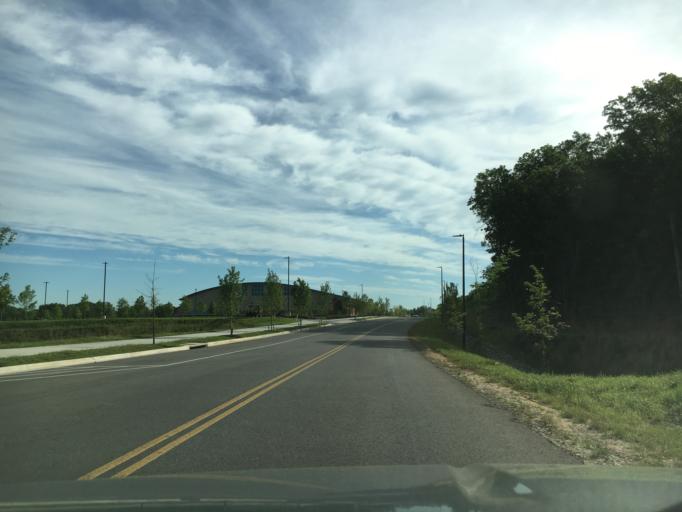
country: US
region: Virginia
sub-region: City of Lynchburg
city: West Lynchburg
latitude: 37.3590
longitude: -79.1638
